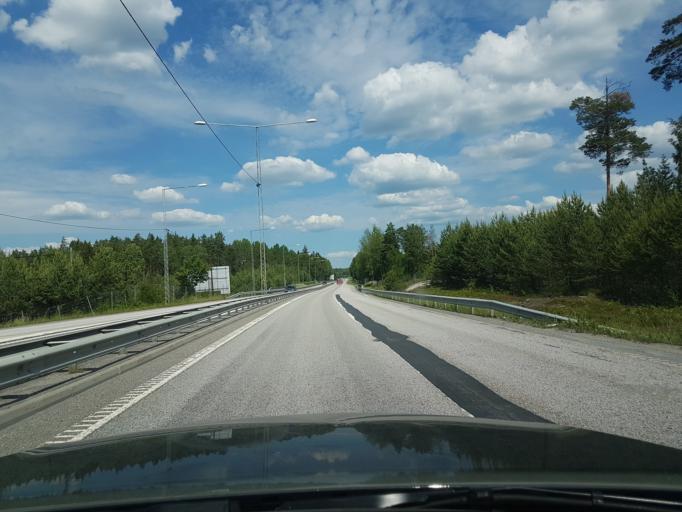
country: SE
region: Stockholm
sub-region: Vallentuna Kommun
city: Vallentuna
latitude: 59.4995
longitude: 18.1661
